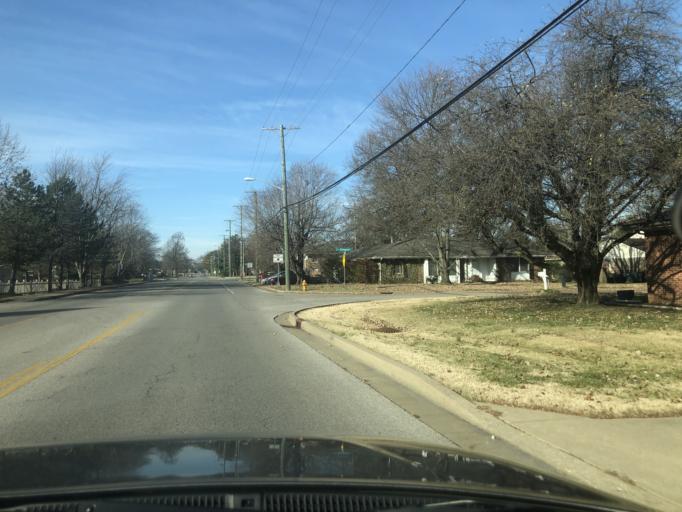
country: US
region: Indiana
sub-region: Warrick County
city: Newburgh
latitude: 37.9695
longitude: -87.4579
